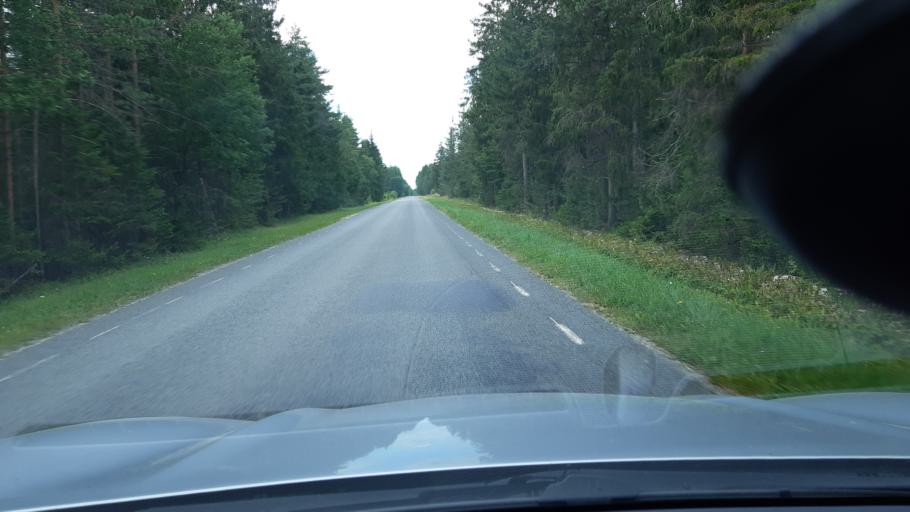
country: EE
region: Raplamaa
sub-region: Rapla vald
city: Rapla
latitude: 58.9003
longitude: 24.6913
